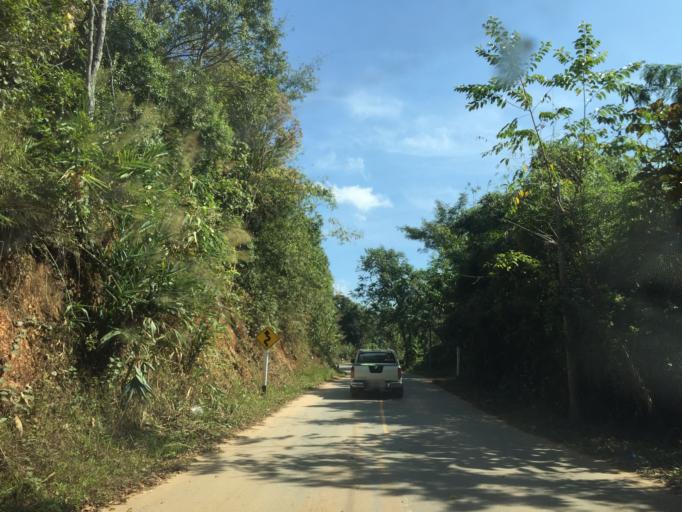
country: TH
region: Chiang Mai
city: Samoeng
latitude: 18.9480
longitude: 98.7942
